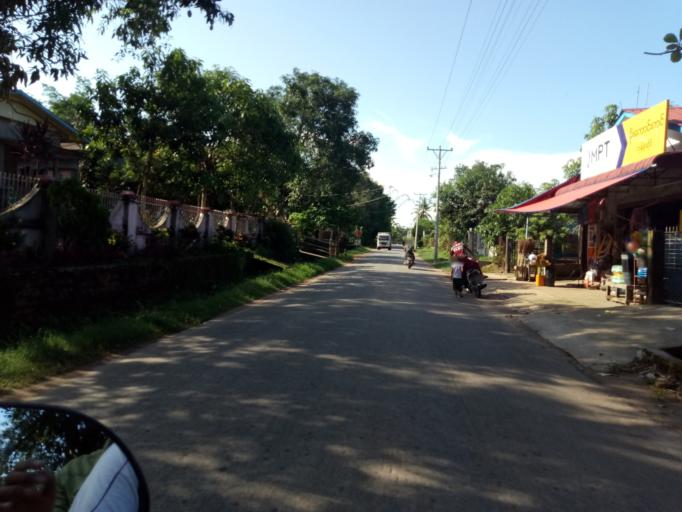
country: MM
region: Mon
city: Mawlamyine
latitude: 16.3966
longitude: 97.5549
